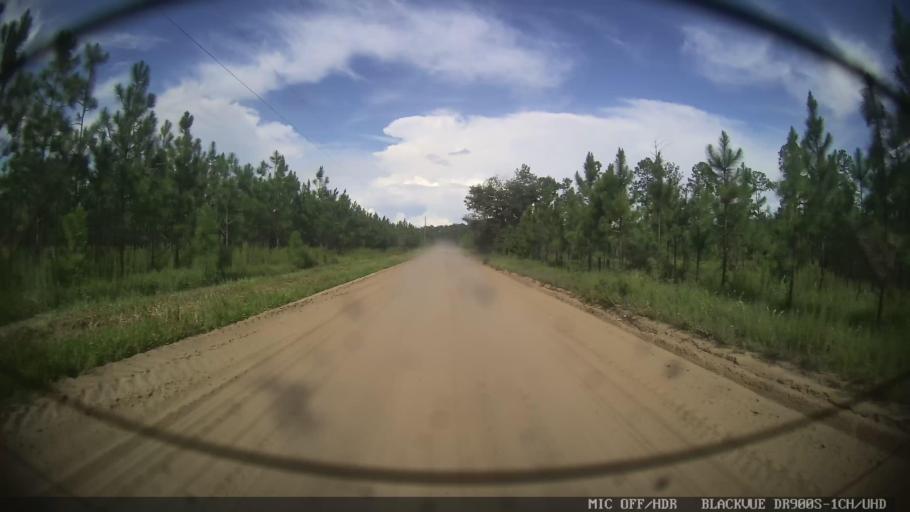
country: US
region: Georgia
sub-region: Echols County
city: Statenville
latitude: 30.6189
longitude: -83.2213
